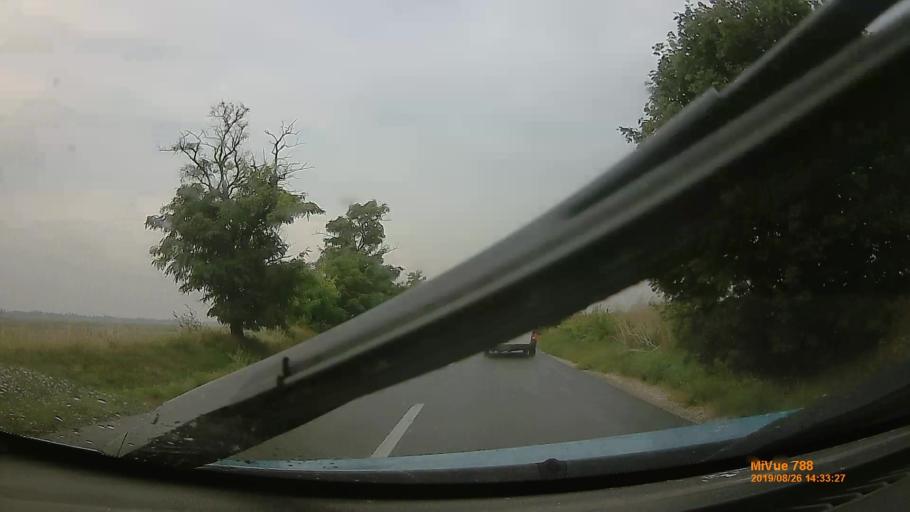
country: HU
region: Fejer
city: Zamoly
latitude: 47.2726
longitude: 18.4201
